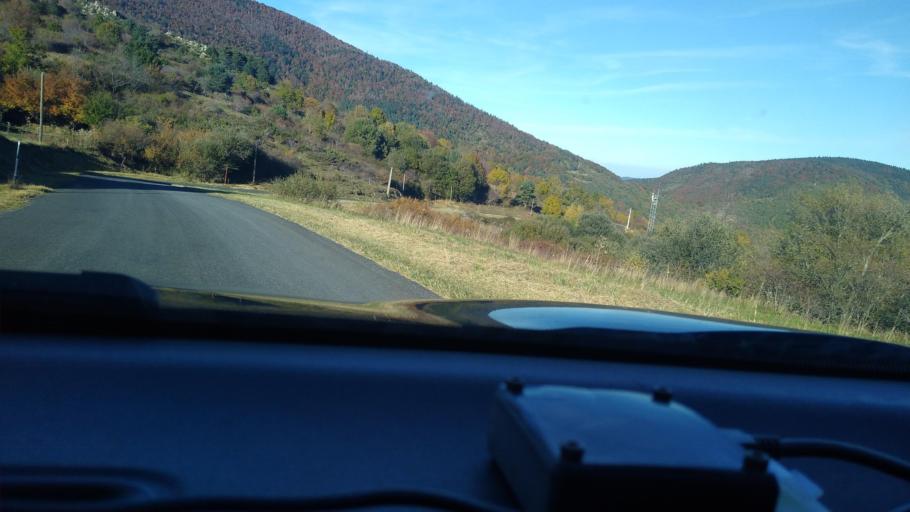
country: FR
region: Languedoc-Roussillon
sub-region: Departement de l'Aude
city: Quillan
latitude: 42.7380
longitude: 2.1539
